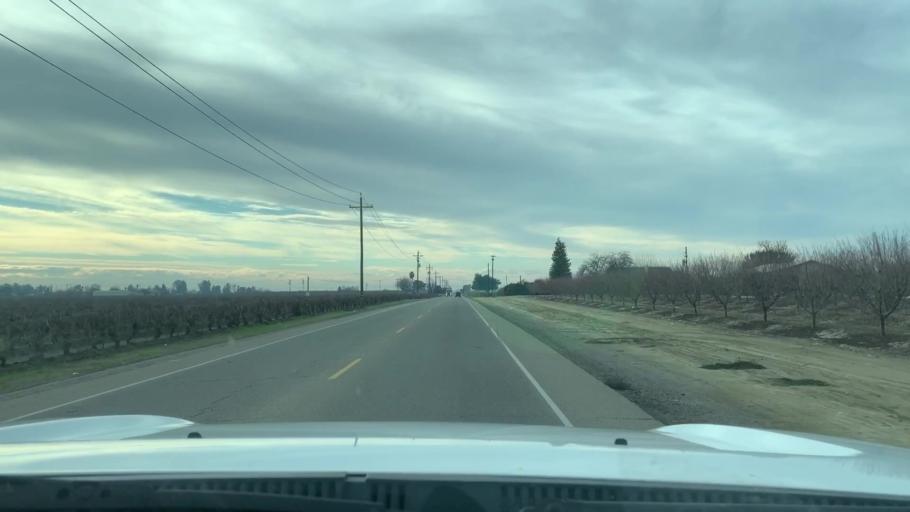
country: US
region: California
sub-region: Fresno County
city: Fowler
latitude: 36.6054
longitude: -119.6752
